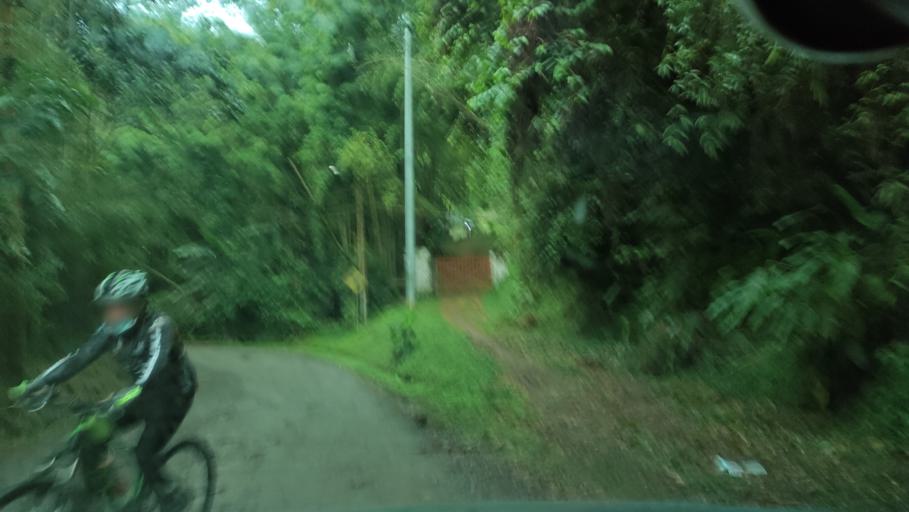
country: CO
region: Valle del Cauca
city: Jamundi
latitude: 3.3251
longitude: -76.6312
